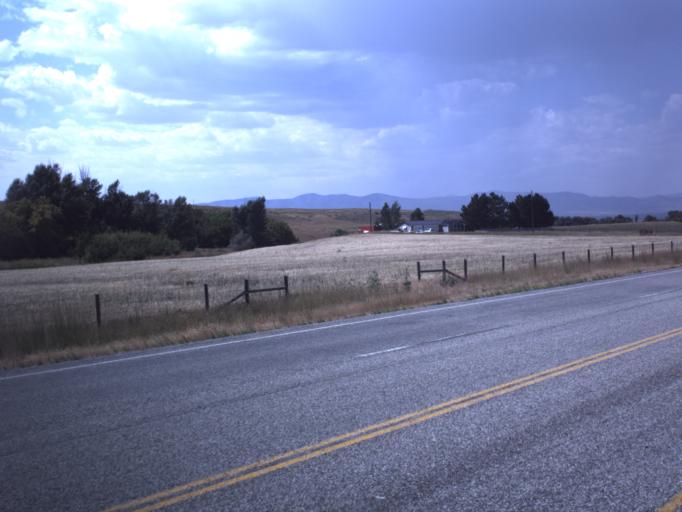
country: US
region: Utah
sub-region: Cache County
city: Mendon
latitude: 41.7882
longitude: -112.0289
